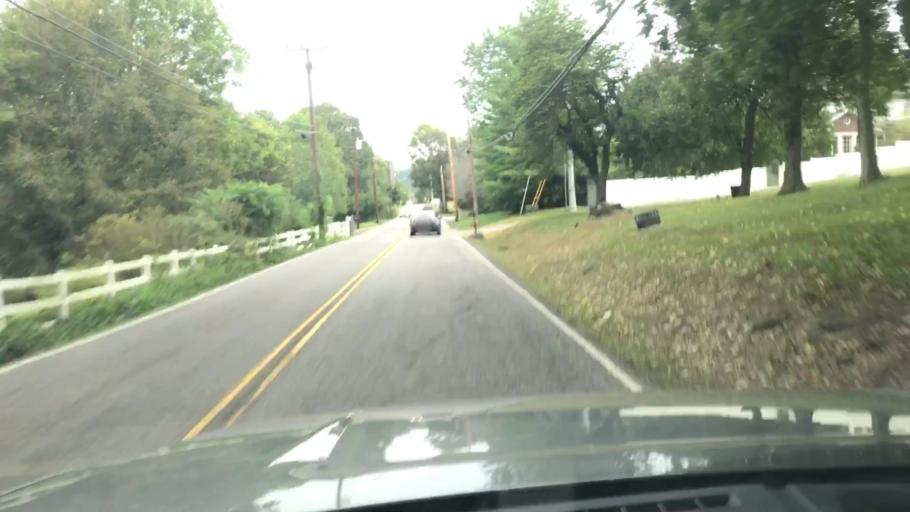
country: US
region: Tennessee
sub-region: Davidson County
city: Forest Hills
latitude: 36.0553
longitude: -86.8158
